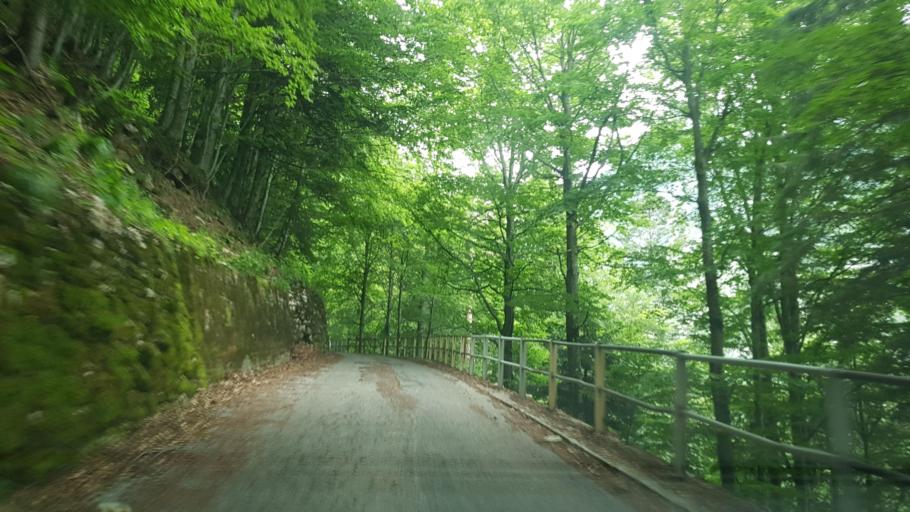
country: IT
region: Friuli Venezia Giulia
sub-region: Provincia di Udine
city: Paularo
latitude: 46.5787
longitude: 13.1346
